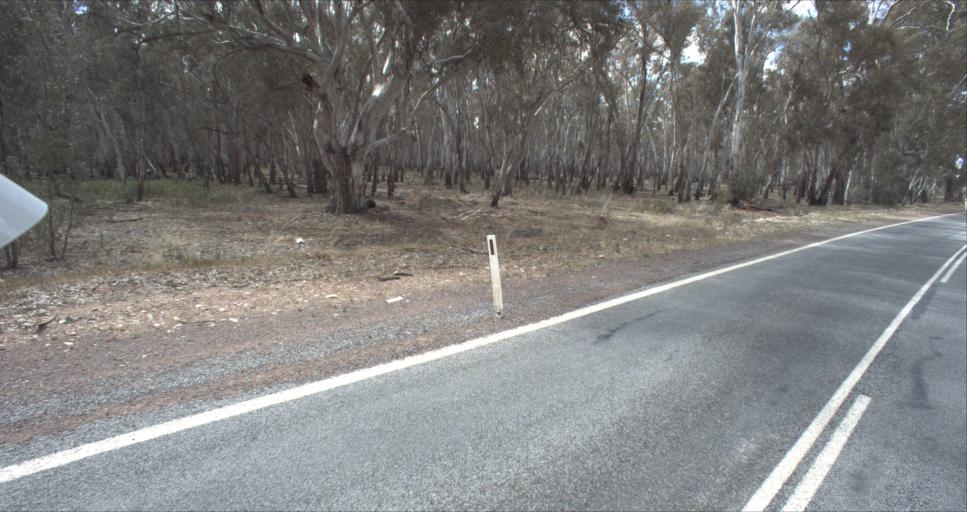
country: AU
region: New South Wales
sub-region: Leeton
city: Leeton
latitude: -34.6246
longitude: 146.3806
